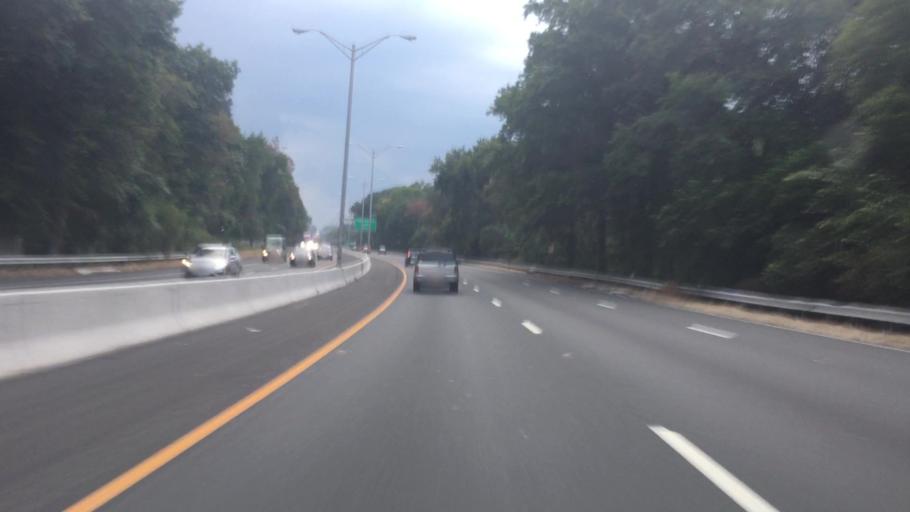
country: US
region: New Jersey
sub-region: Bergen County
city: Midland Park
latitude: 40.9822
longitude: -74.1619
